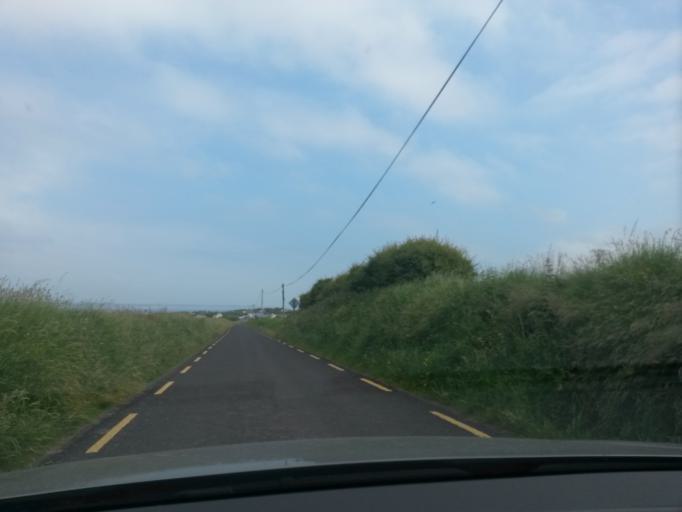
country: IE
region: Munster
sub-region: Ciarrai
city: Ballybunnion
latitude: 52.5692
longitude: -9.6349
